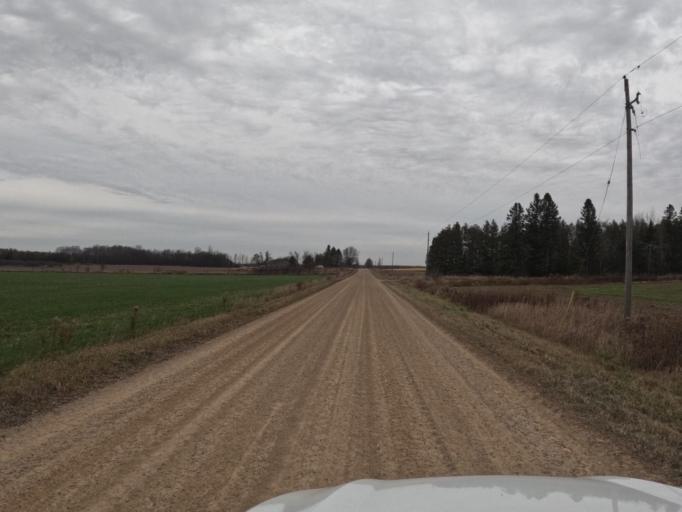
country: CA
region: Ontario
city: Shelburne
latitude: 44.0228
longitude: -80.3695
